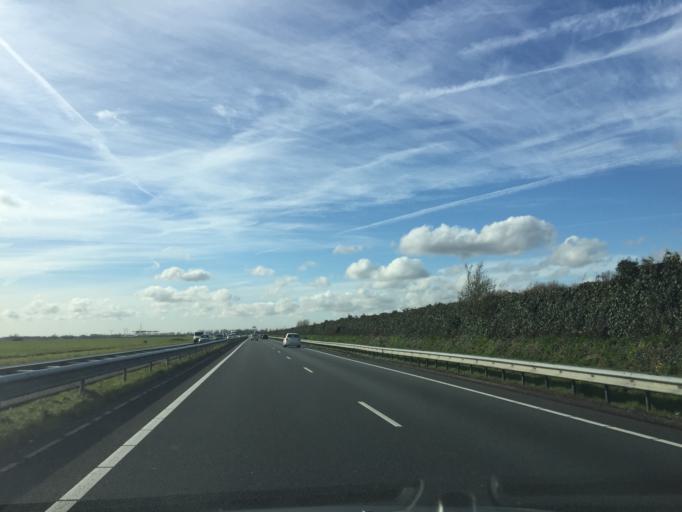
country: NL
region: South Holland
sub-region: Bodegraven-Reeuwijk
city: Bodegraven
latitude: 52.1033
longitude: 4.7125
